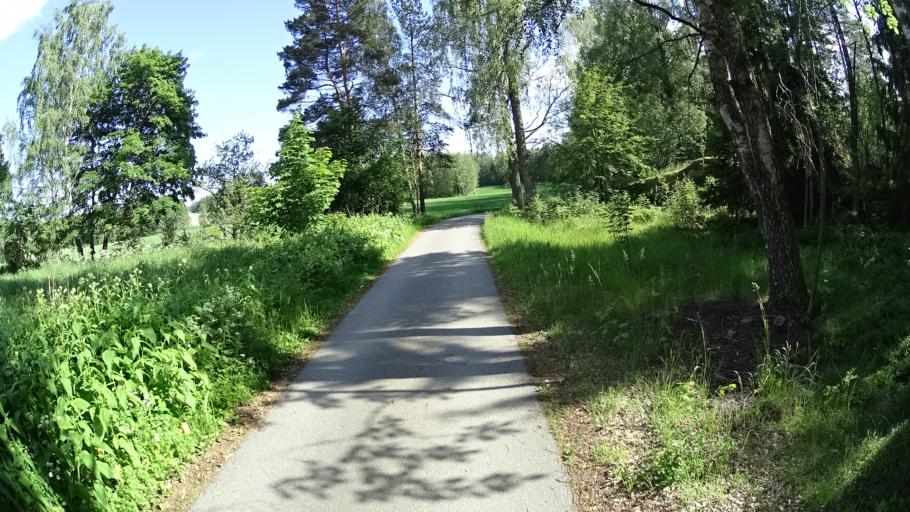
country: FI
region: Uusimaa
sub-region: Helsinki
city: Vantaa
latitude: 60.2386
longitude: 25.1822
